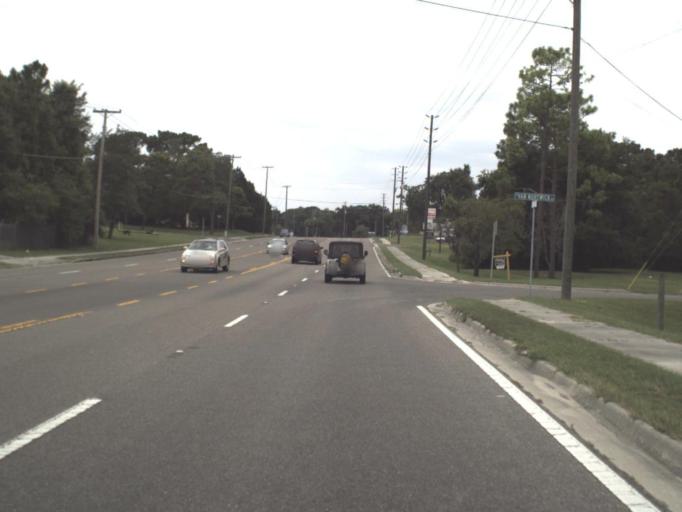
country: US
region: Florida
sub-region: Citrus County
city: Lecanto
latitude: 28.8785
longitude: -82.5248
